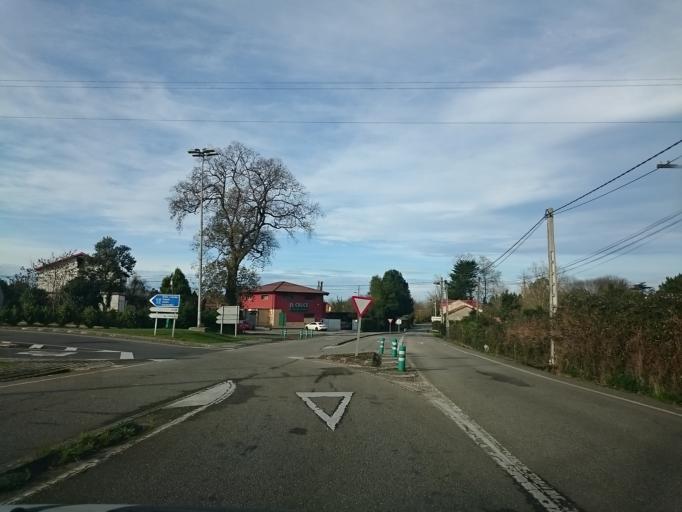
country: ES
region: Asturias
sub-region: Province of Asturias
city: Gijon
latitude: 43.5144
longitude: -5.6207
